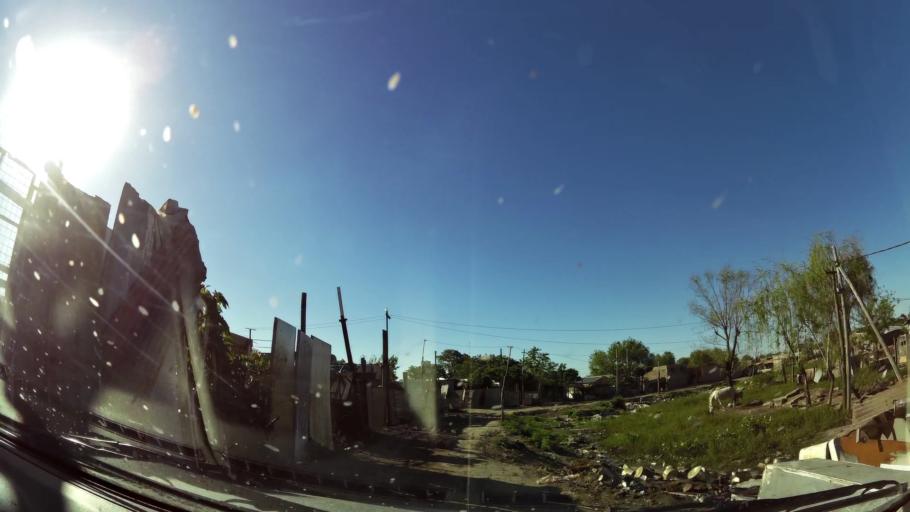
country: AR
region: Buenos Aires
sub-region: Partido de Quilmes
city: Quilmes
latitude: -34.7535
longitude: -58.3198
